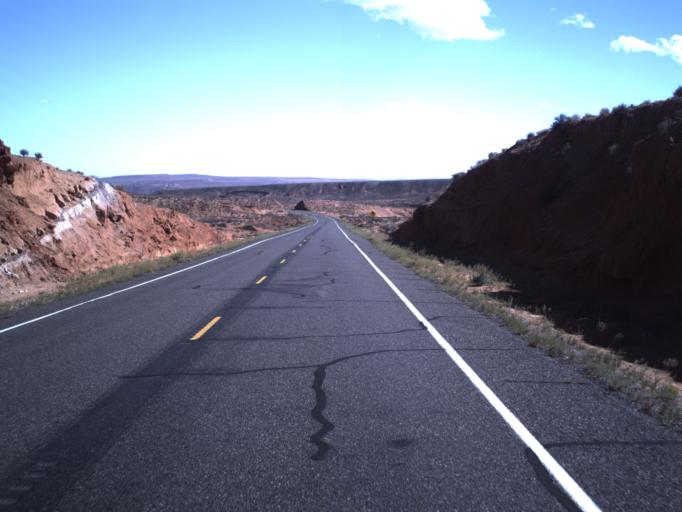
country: US
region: Utah
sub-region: Wayne County
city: Loa
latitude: 38.0744
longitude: -110.6089
